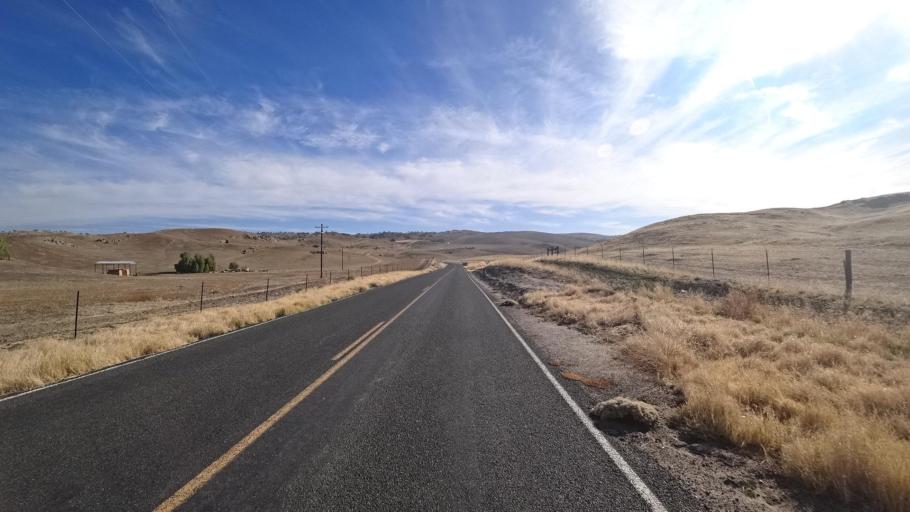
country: US
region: California
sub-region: Kern County
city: Oildale
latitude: 35.6122
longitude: -118.8793
